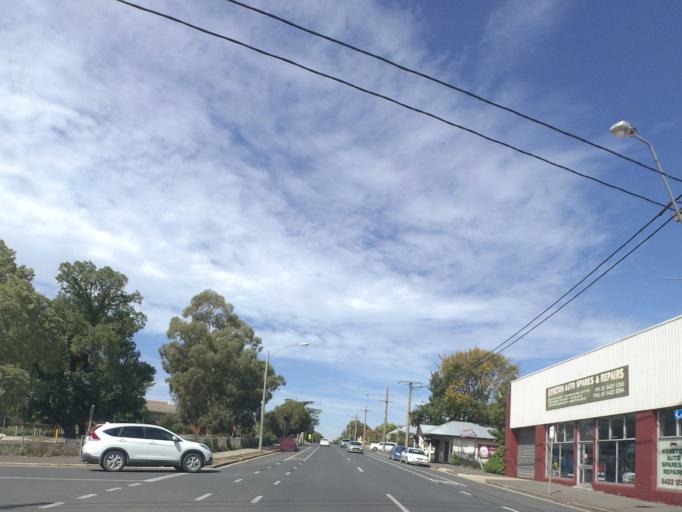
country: AU
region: Victoria
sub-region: Mount Alexander
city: Castlemaine
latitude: -37.2509
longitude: 144.4565
